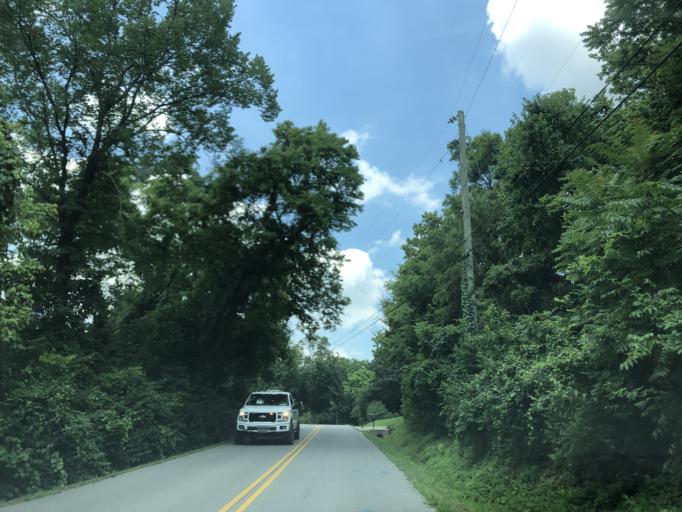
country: US
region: Tennessee
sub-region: Williamson County
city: Brentwood Estates
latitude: 36.0220
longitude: -86.7298
